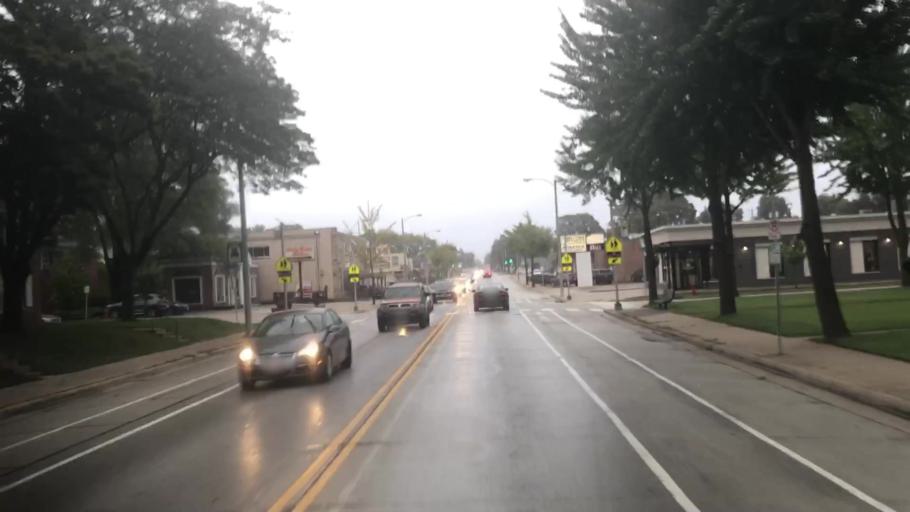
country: US
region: Wisconsin
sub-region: Milwaukee County
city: Wauwatosa
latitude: 43.0605
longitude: -88.0256
